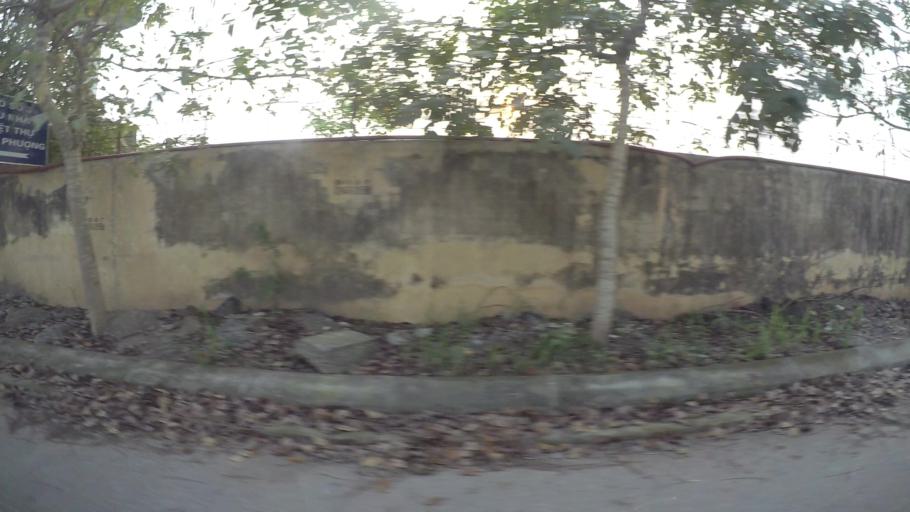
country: VN
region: Ha Noi
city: Cau Dien
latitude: 21.0022
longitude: 105.7274
